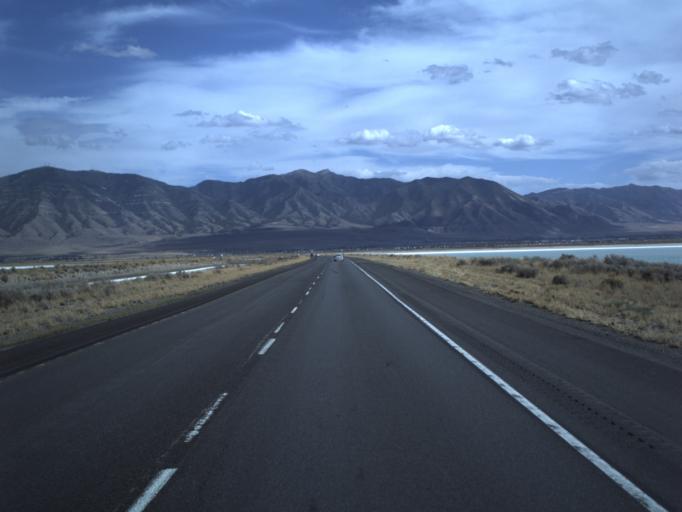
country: US
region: Utah
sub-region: Tooele County
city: Stansbury park
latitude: 40.6675
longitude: -112.3758
